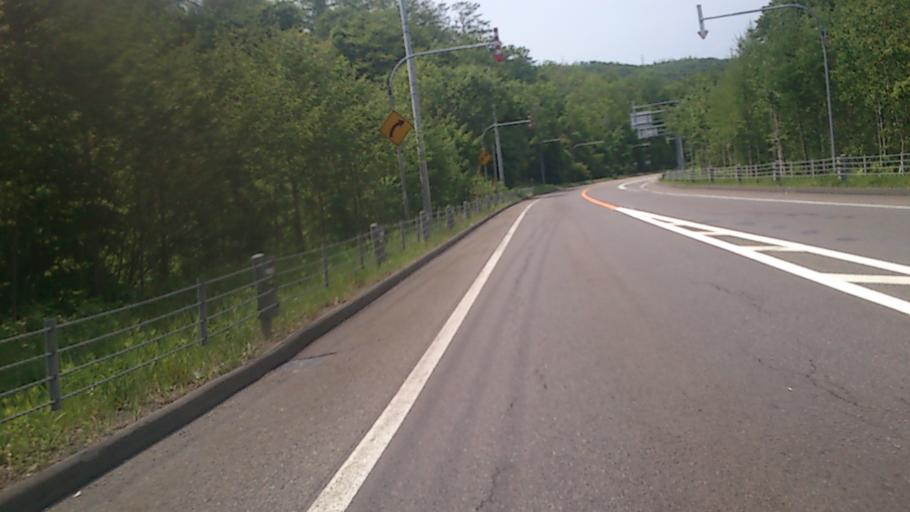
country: JP
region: Hokkaido
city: Otofuke
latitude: 43.2285
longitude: 143.5294
